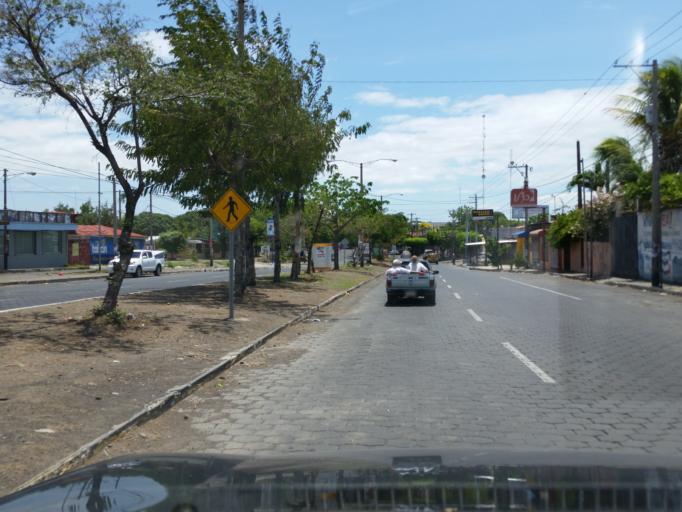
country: NI
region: Managua
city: Managua
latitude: 12.1440
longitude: -86.2265
